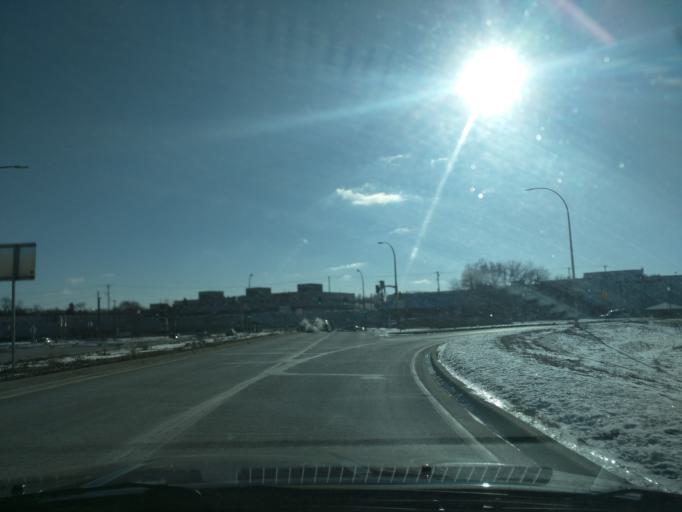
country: US
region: Minnesota
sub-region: Hennepin County
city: Minnetonka Mills
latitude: 44.9249
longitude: -93.3997
